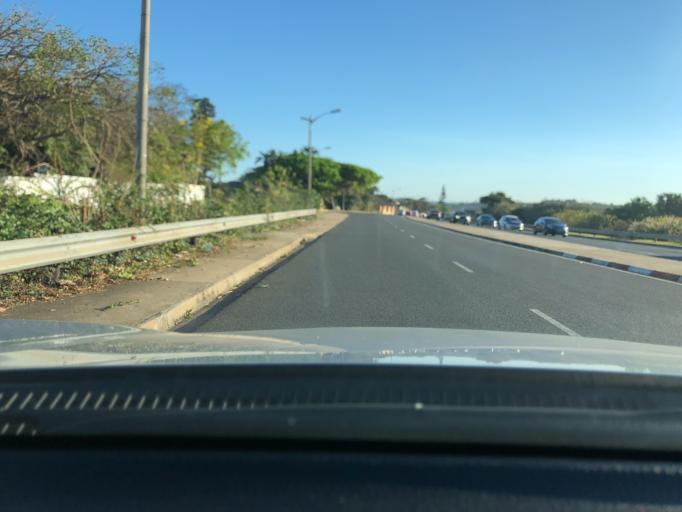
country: ZA
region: KwaZulu-Natal
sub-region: eThekwini Metropolitan Municipality
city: Umkomaas
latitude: -30.0381
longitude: 30.8986
